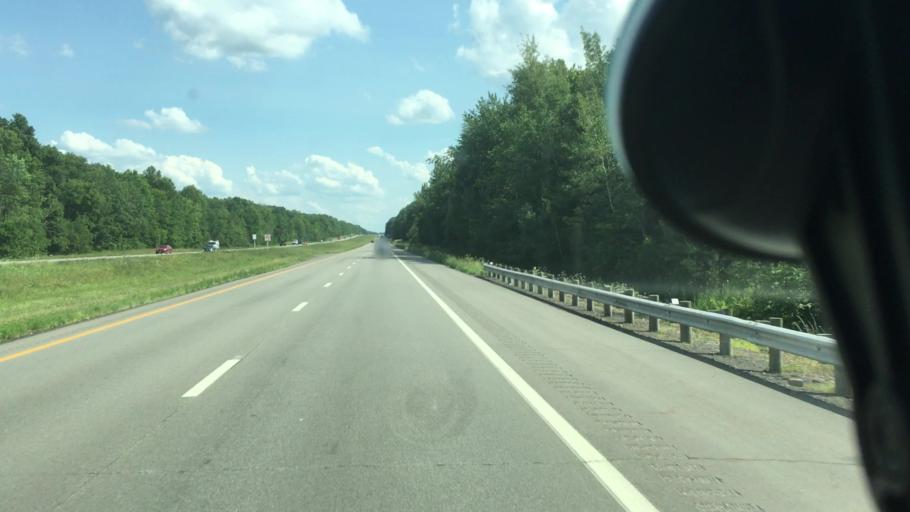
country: US
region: Ohio
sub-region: Mahoning County
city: Canfield
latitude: 41.0623
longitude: -80.7506
